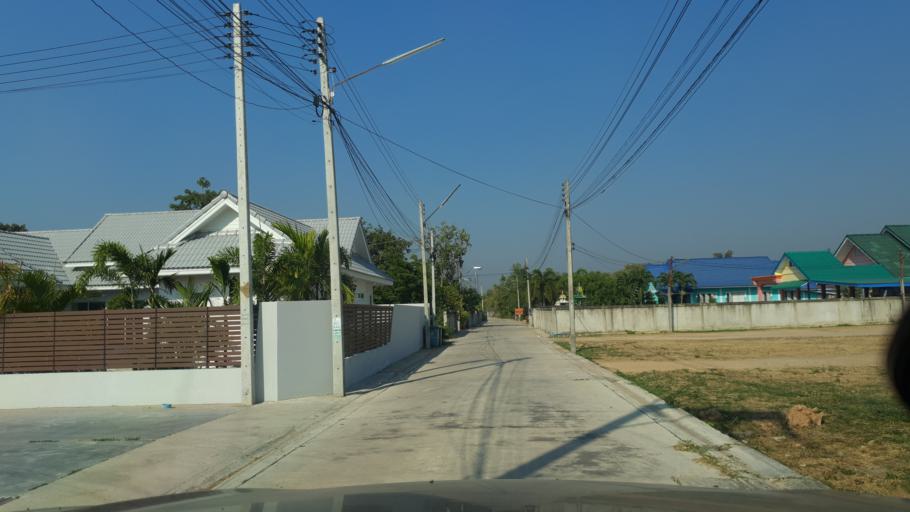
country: TH
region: Phetchaburi
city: Cha-am
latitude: 12.7855
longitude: 99.9772
